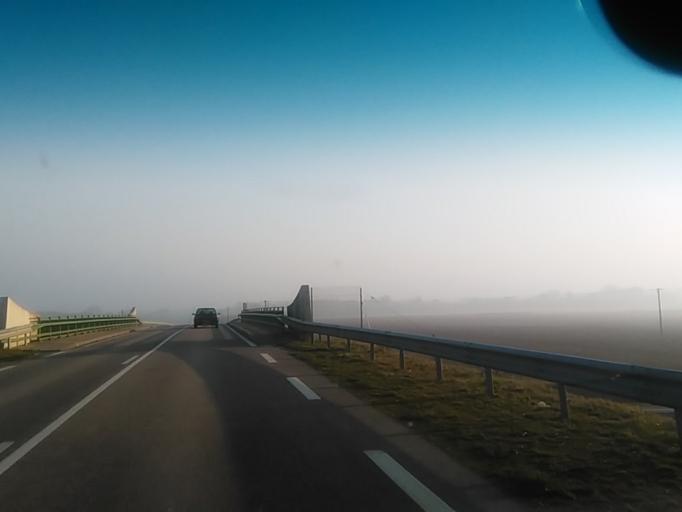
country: FR
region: Lower Normandy
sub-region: Departement du Calvados
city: Falaise
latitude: 48.8735
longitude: -0.2151
